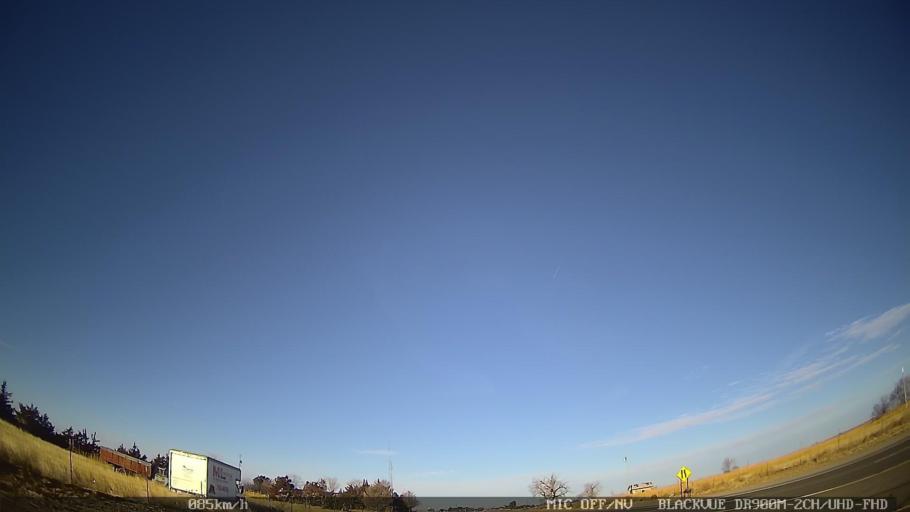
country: US
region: New Mexico
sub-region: Curry County
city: Clovis
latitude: 34.4340
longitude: -103.2404
